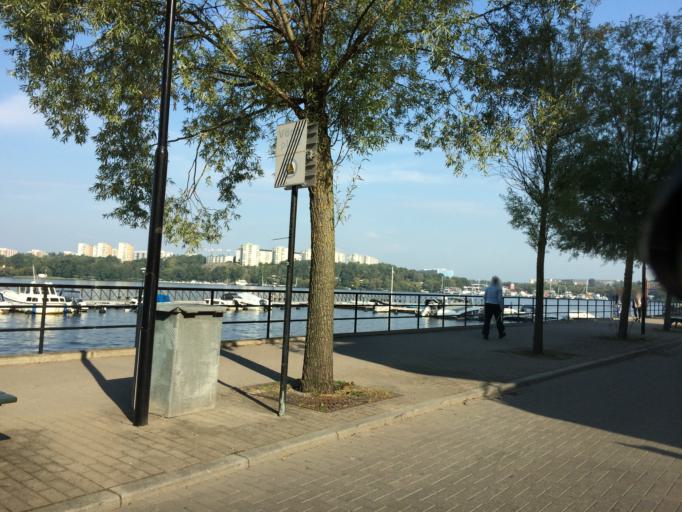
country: SE
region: Stockholm
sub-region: Solna Kommun
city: Solna
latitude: 59.3369
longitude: 17.9978
